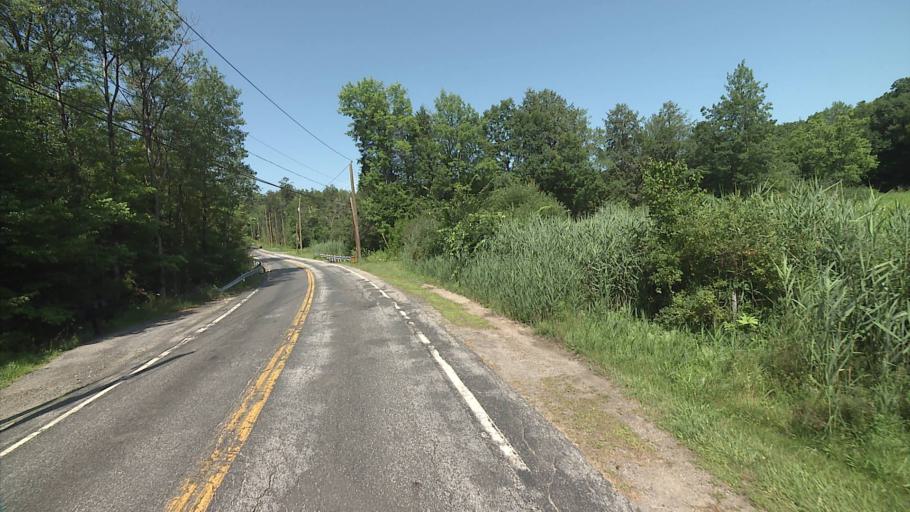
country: US
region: Connecticut
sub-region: Litchfield County
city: Winchester Center
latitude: 41.9199
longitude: -73.1977
